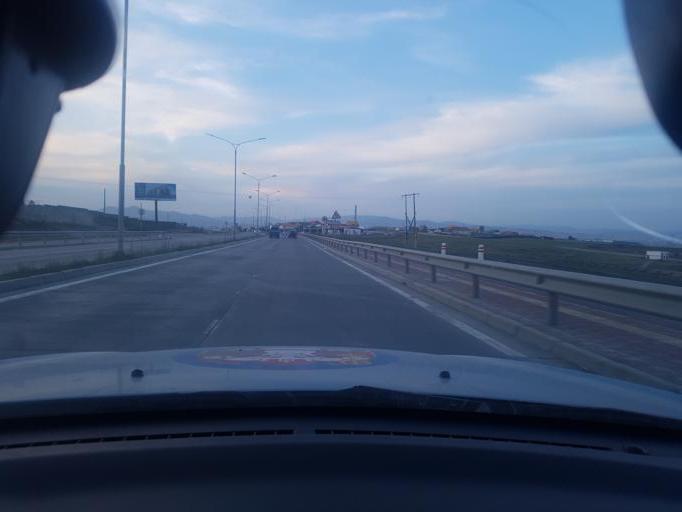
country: MN
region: Ulaanbaatar
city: Ulaanbaatar
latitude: 47.8602
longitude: 106.7879
